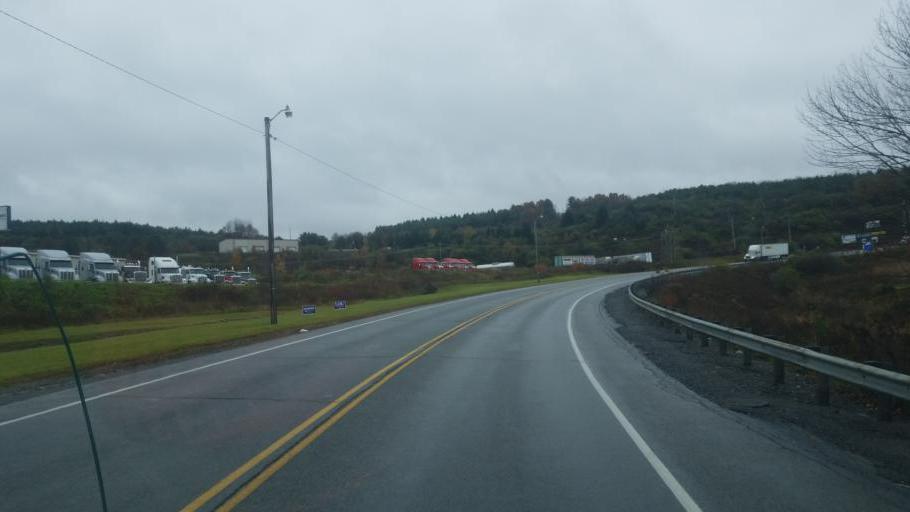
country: US
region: Pennsylvania
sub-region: Clearfield County
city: Clearfield
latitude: 41.0429
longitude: -78.3974
